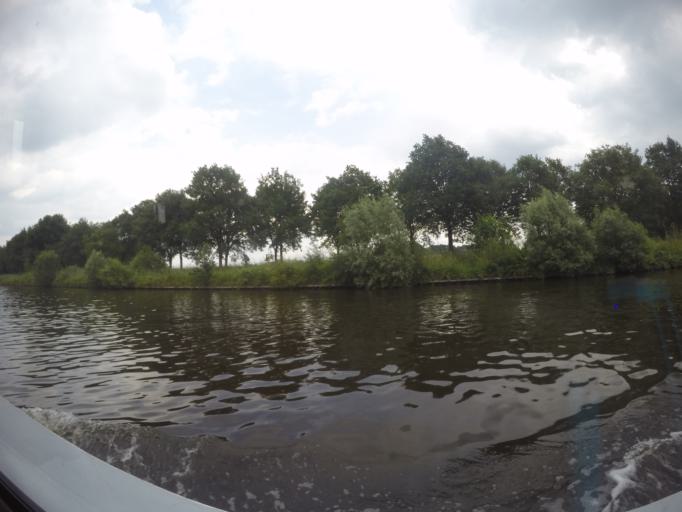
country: NL
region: Overijssel
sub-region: Gemeente Hof van Twente
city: Hengevelde
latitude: 52.2603
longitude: 6.6463
